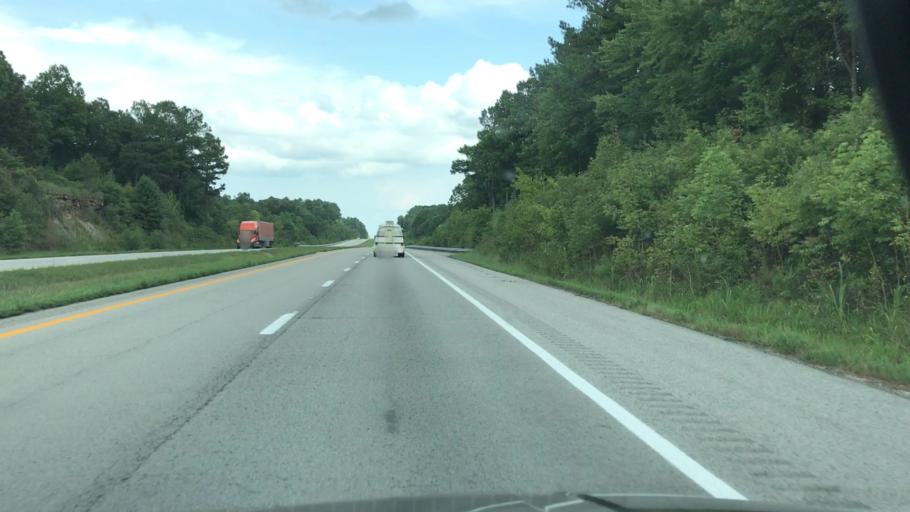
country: US
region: Kentucky
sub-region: Hopkins County
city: Dawson Springs
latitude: 37.1959
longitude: -87.6430
